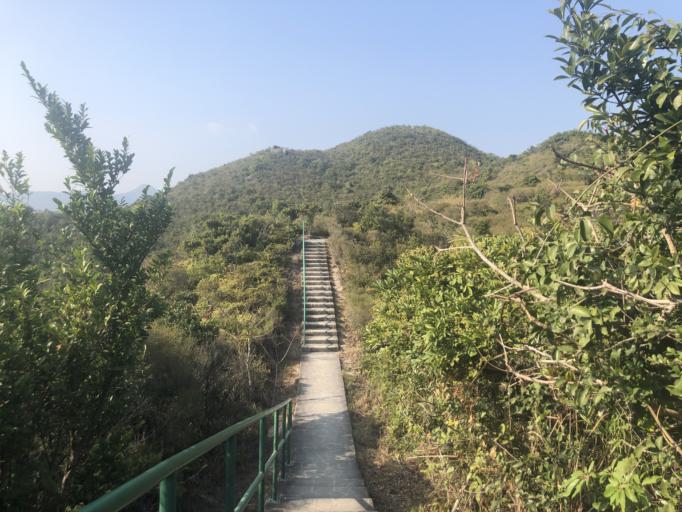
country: HK
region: Sai Kung
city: Sai Kung
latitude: 22.3579
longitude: 114.2955
